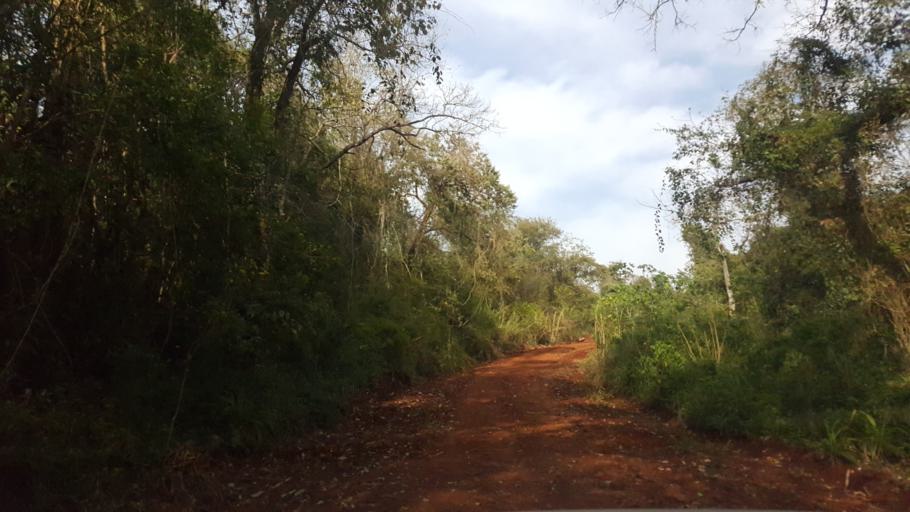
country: AR
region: Misiones
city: Capiovi
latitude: -26.9050
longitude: -55.1159
